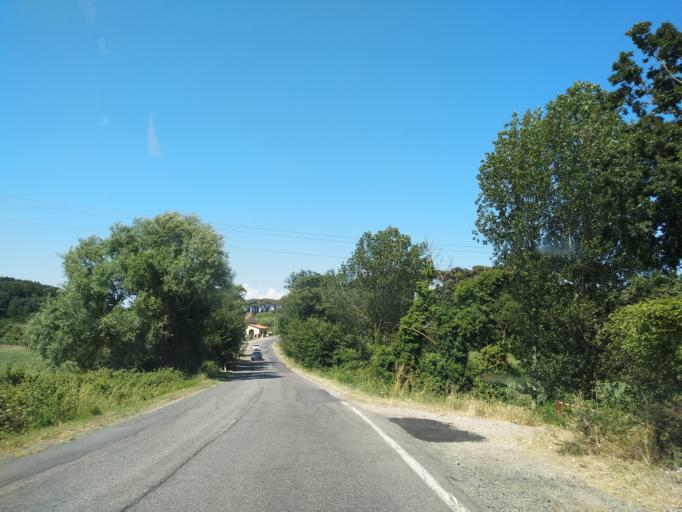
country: IT
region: Tuscany
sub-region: Provincia di Livorno
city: Livorno
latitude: 43.5661
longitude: 10.3604
